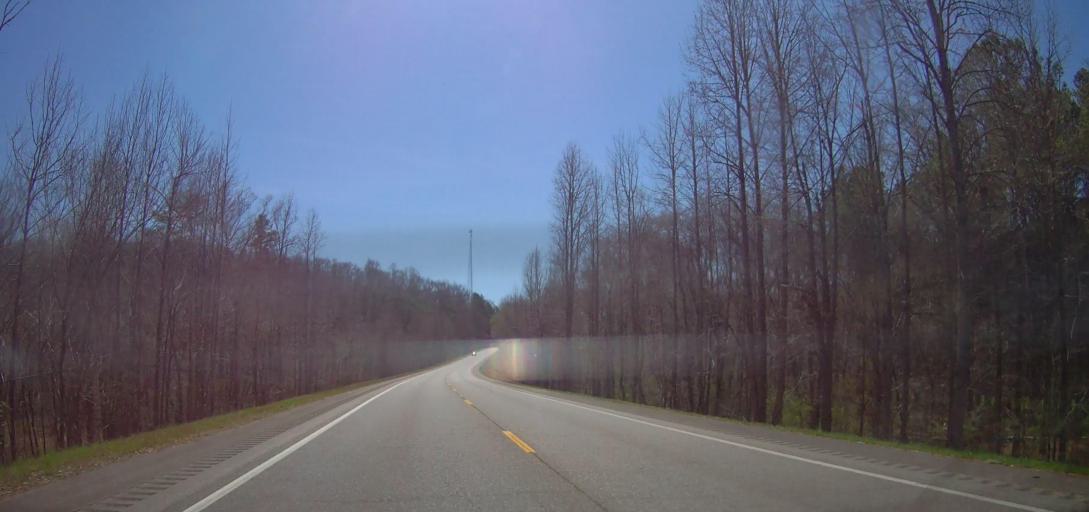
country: US
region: Alabama
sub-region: Calhoun County
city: Ohatchee
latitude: 33.7922
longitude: -86.0358
